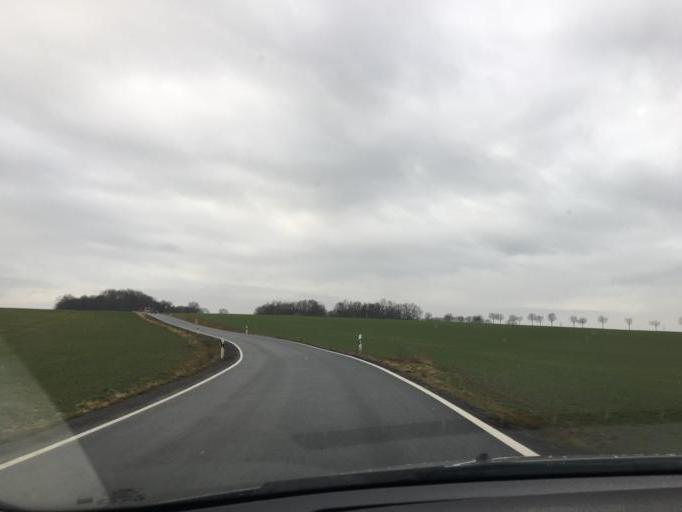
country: DE
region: Saxony
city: Pfaffroda
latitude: 50.8556
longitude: 12.5305
